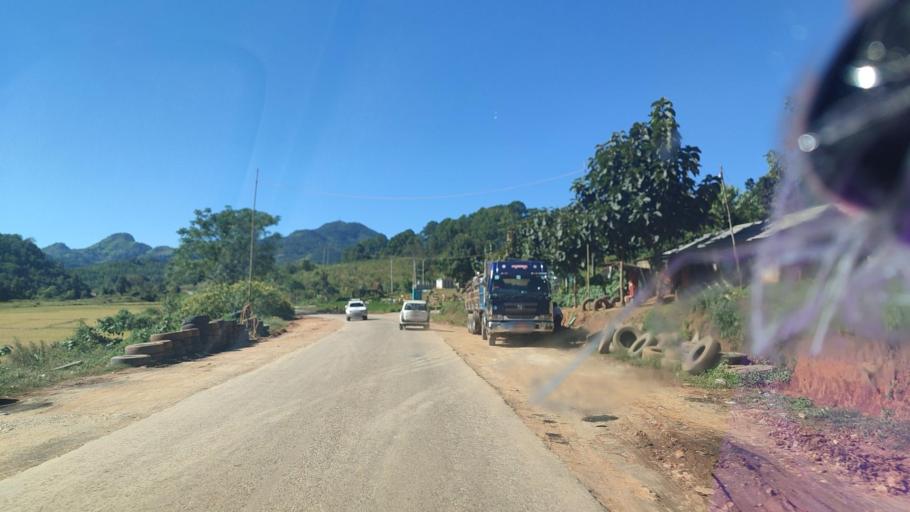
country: MM
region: Shan
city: Taunggyi
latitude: 20.8947
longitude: 97.5531
